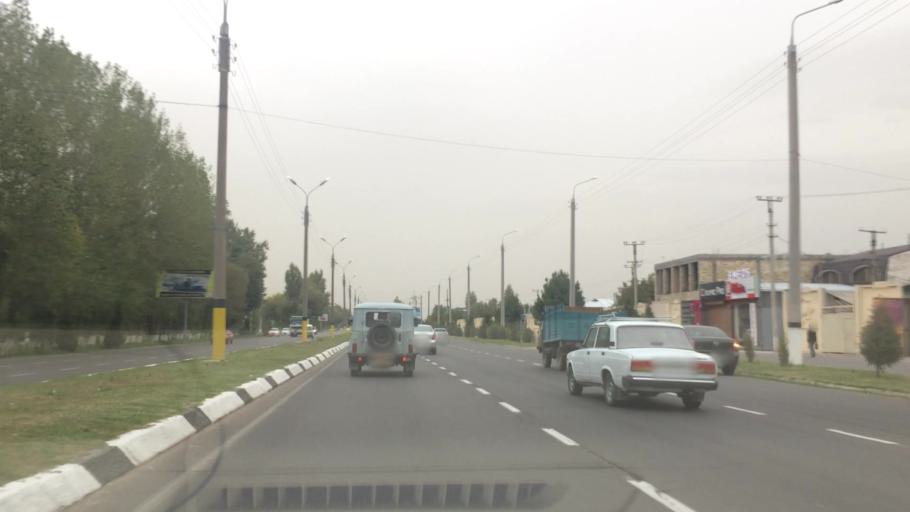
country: UZ
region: Toshkent
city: Salor
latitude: 41.3170
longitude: 69.3564
